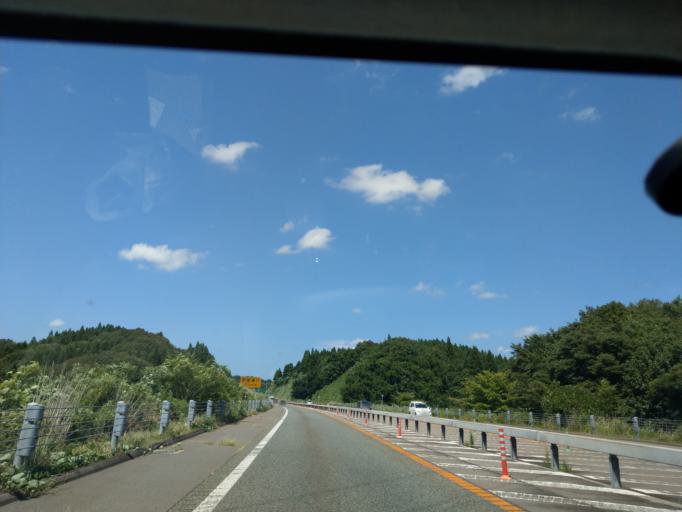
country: JP
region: Akita
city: Akita
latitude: 39.6695
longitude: 140.1882
